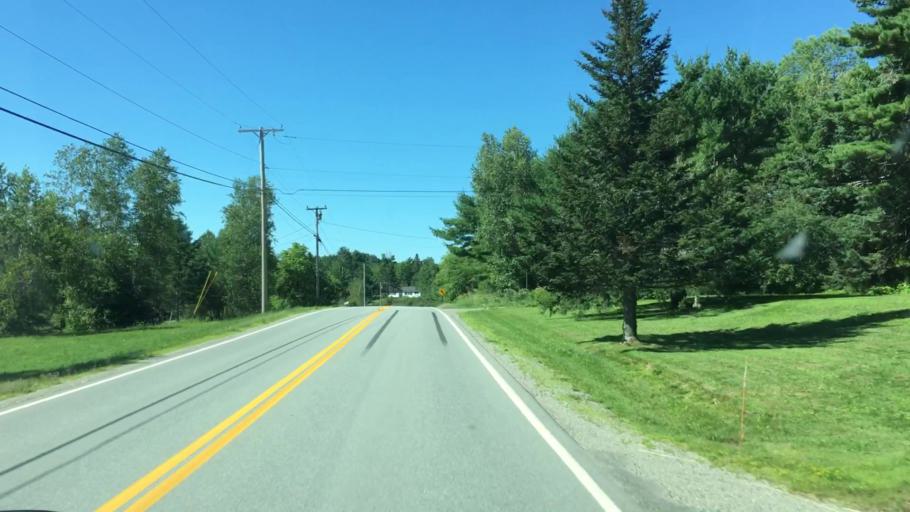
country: US
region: Maine
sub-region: Hancock County
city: Dedham
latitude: 44.7111
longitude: -68.6486
